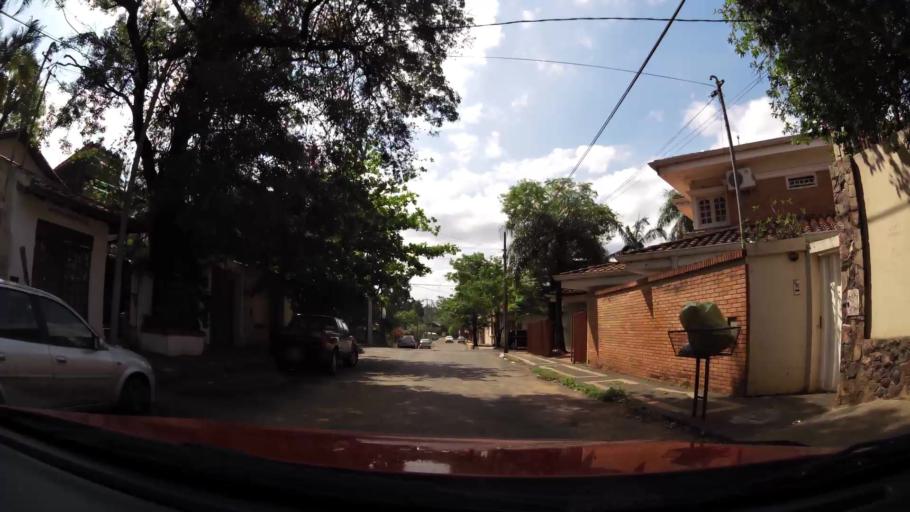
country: PY
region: Central
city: Fernando de la Mora
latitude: -25.3436
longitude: -57.5160
